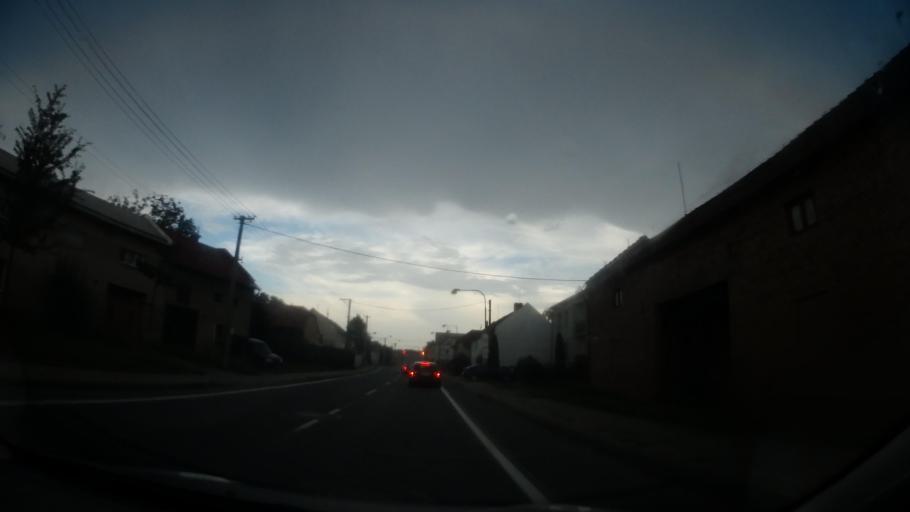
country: CZ
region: Olomoucky
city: Horka nad Moravou
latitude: 49.6409
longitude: 17.2311
